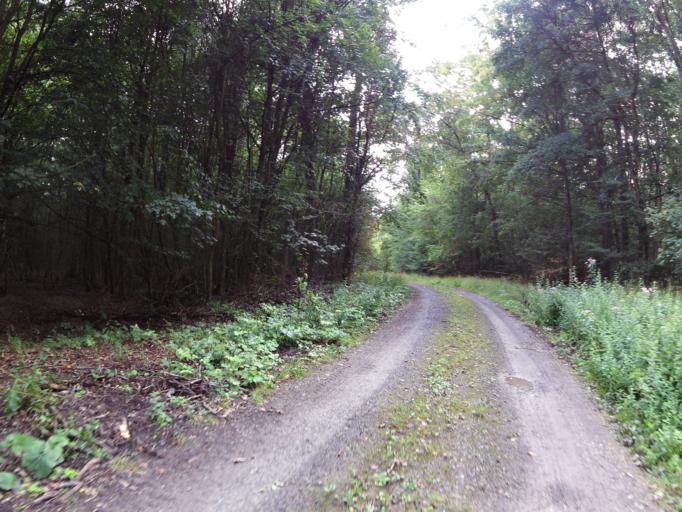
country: DE
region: Bavaria
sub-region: Regierungsbezirk Unterfranken
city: Margetshochheim
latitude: 49.8289
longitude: 9.8367
